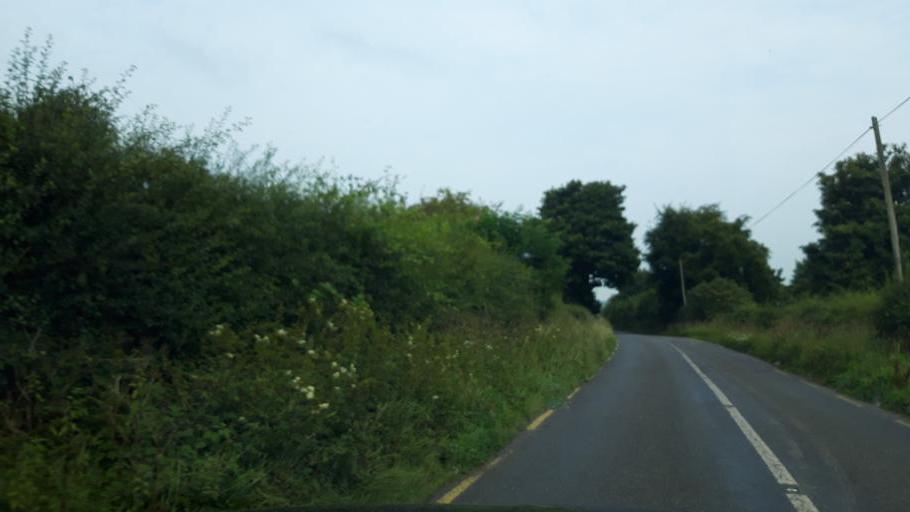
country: IE
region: Leinster
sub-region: Kilkenny
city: Callan
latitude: 52.5399
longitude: -7.5229
